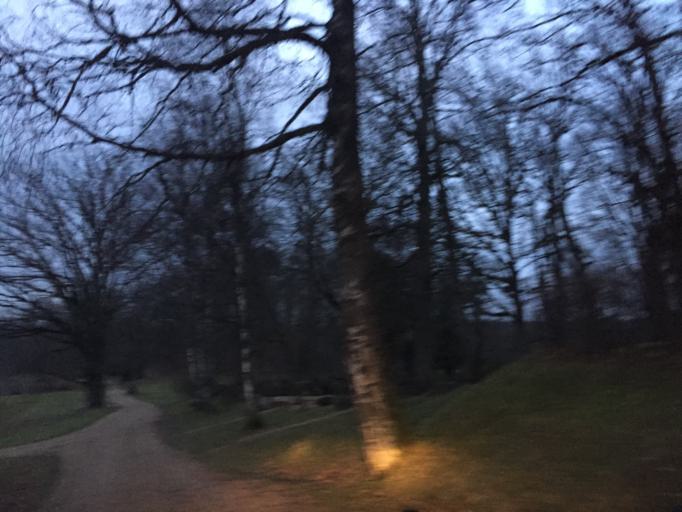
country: LV
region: Amatas Novads
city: Drabesi
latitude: 57.0708
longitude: 25.1984
